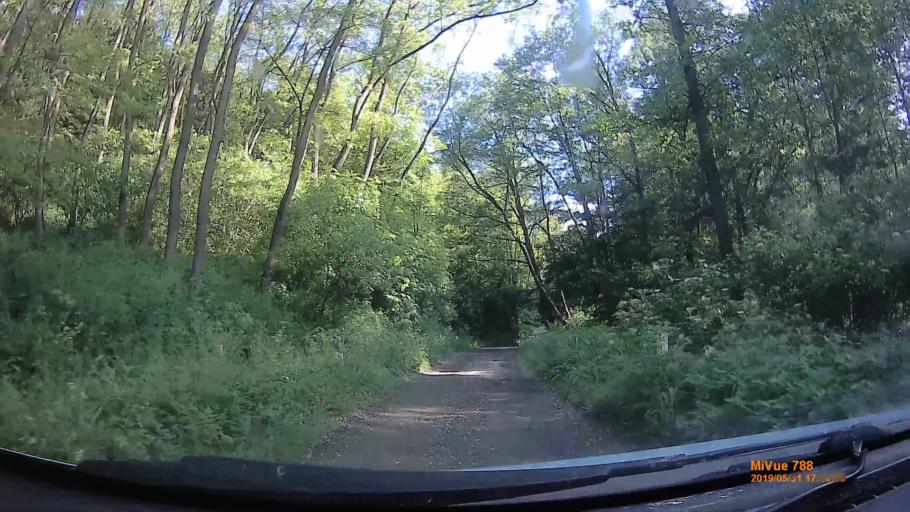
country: HU
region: Nograd
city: Nagyoroszi
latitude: 48.0333
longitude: 19.0469
